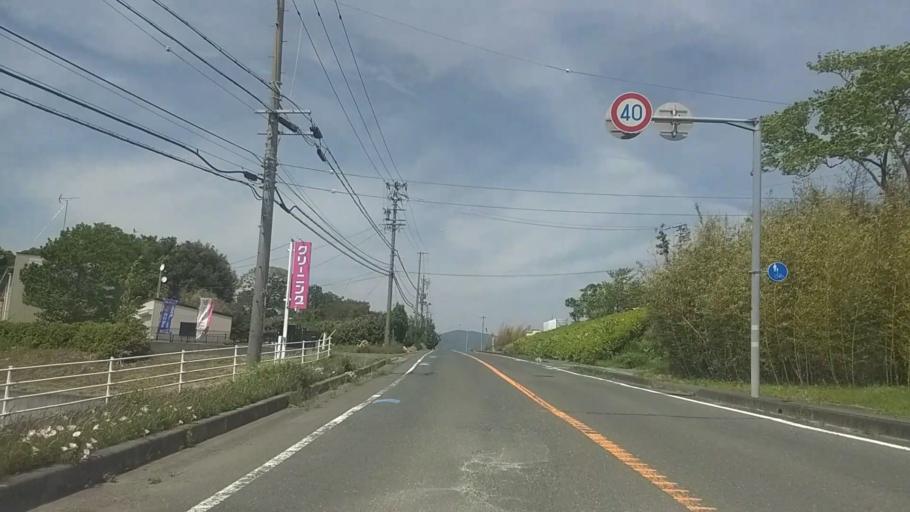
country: JP
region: Shizuoka
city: Kosai-shi
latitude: 34.7881
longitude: 137.5452
